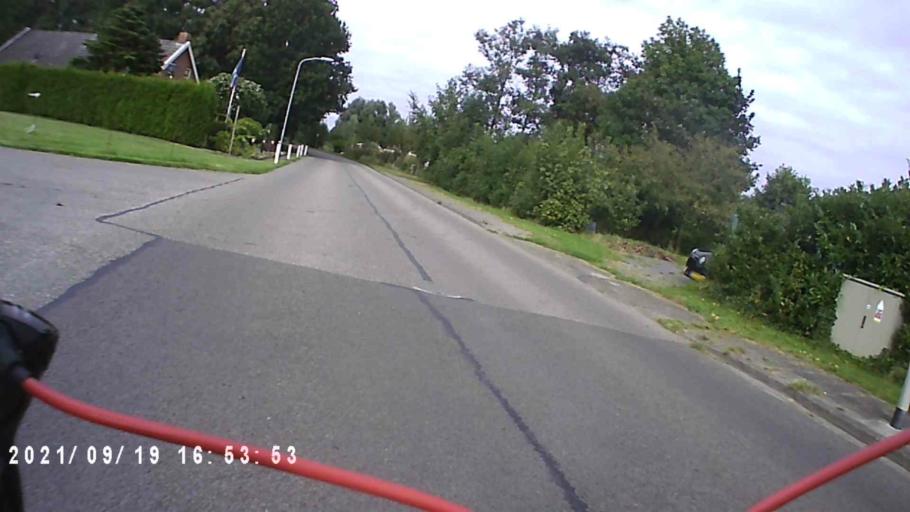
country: NL
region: Groningen
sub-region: Gemeente  Oldambt
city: Winschoten
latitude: 53.1851
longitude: 7.0784
